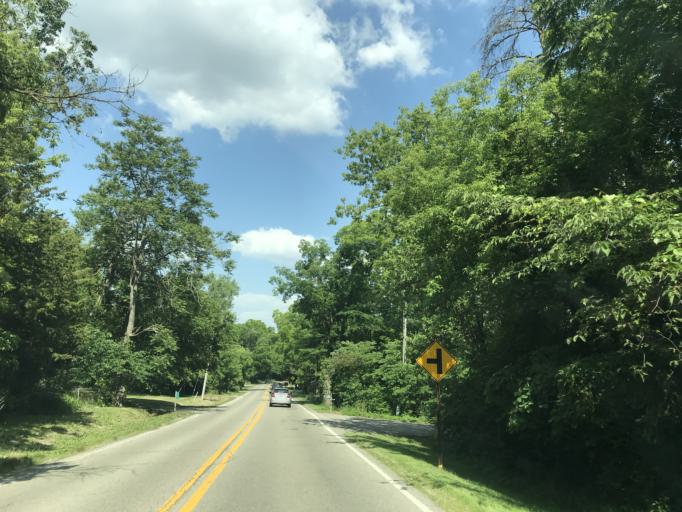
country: US
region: Michigan
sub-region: Washtenaw County
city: Ypsilanti
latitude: 42.2790
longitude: -83.6497
